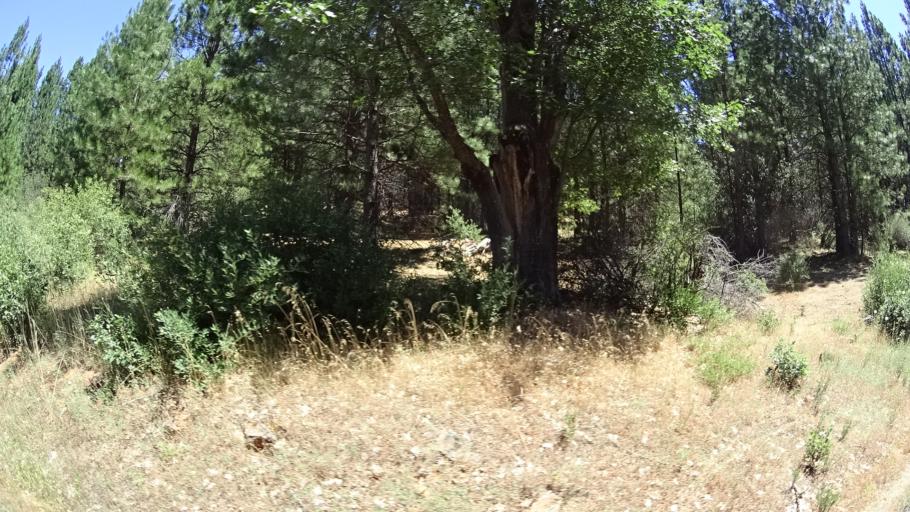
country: US
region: California
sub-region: Calaveras County
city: Mountain Ranch
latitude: 38.2717
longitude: -120.4648
